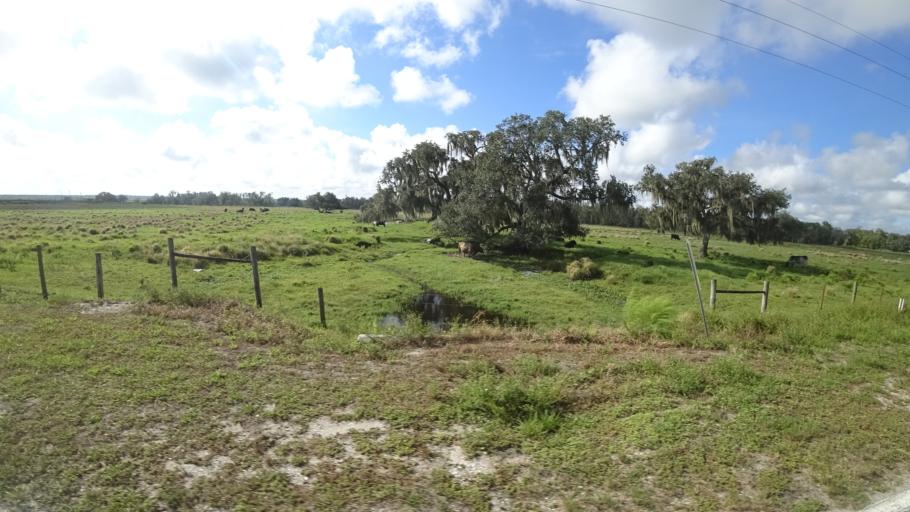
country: US
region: Florida
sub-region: Sarasota County
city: Lake Sarasota
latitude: 27.3460
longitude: -82.2385
